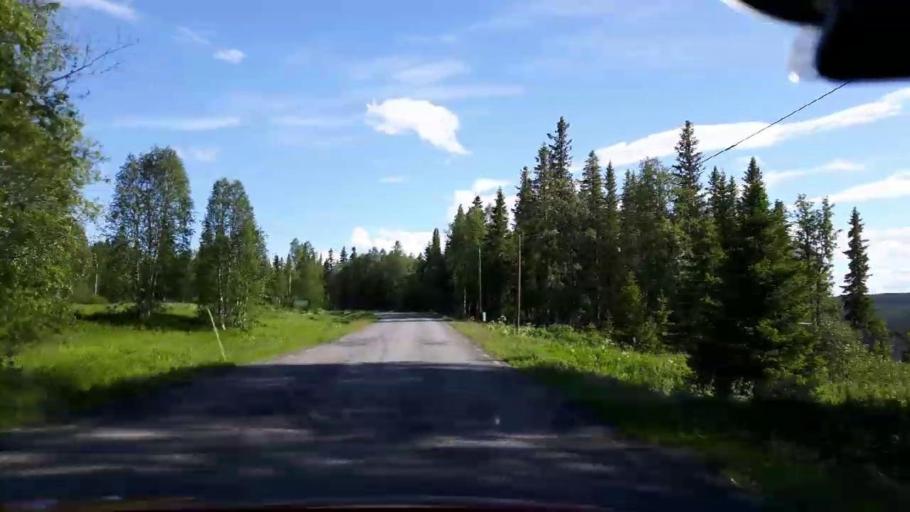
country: SE
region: Jaemtland
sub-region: Krokoms Kommun
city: Valla
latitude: 63.7038
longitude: 14.1465
